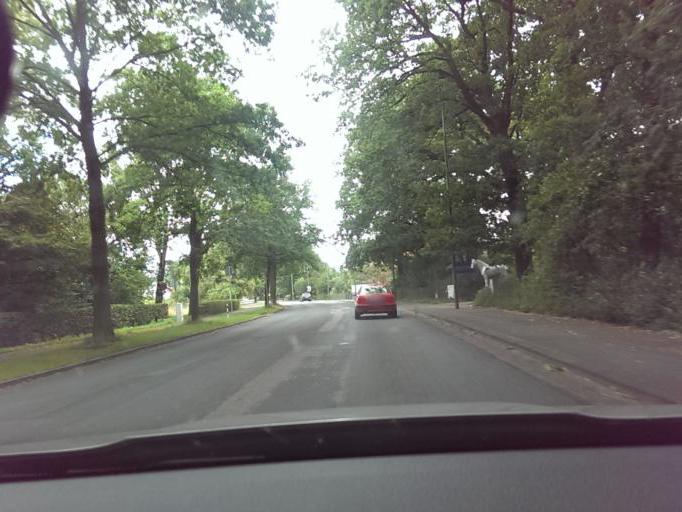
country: DE
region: Lower Saxony
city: Langenhagen
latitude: 52.4653
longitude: 9.7374
